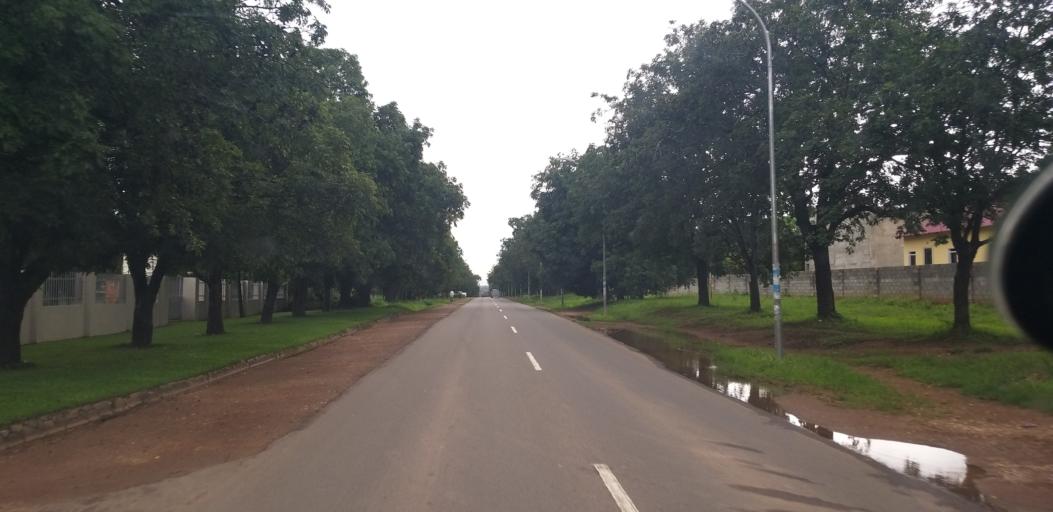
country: ZM
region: Lusaka
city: Lusaka
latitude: -15.4319
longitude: 28.3465
